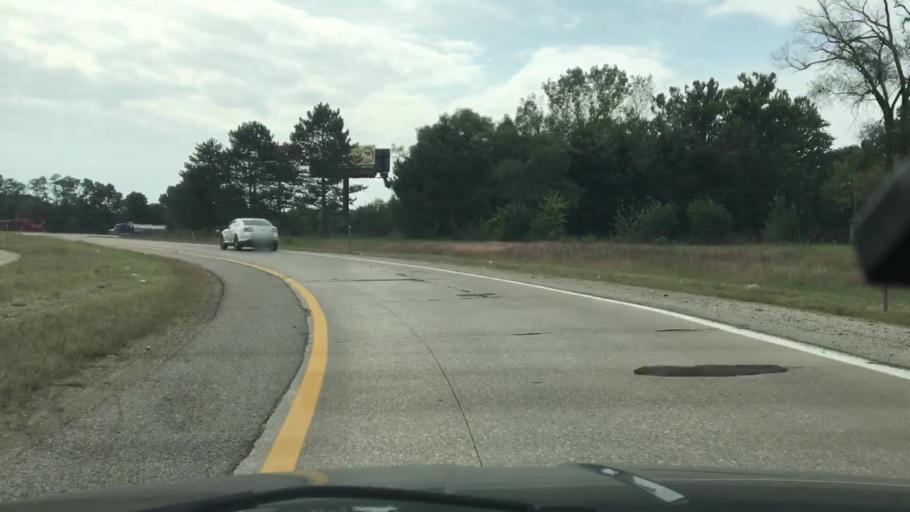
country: US
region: Michigan
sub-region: Berrien County
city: Fair Plain
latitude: 42.0691
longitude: -86.4388
